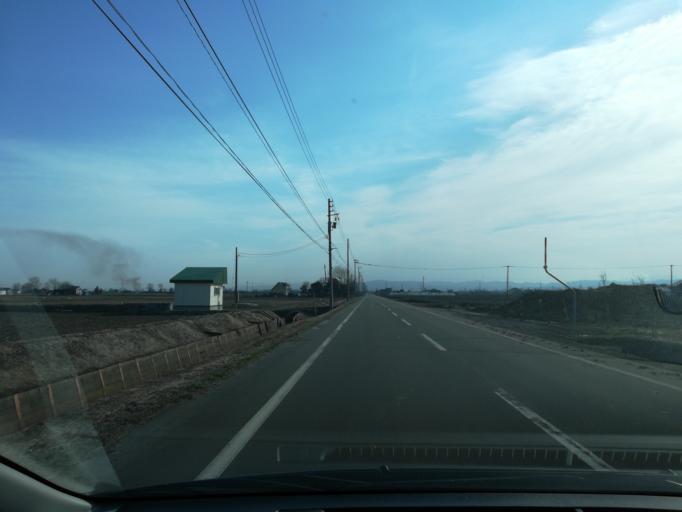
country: JP
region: Hokkaido
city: Iwamizawa
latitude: 43.1811
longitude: 141.6891
